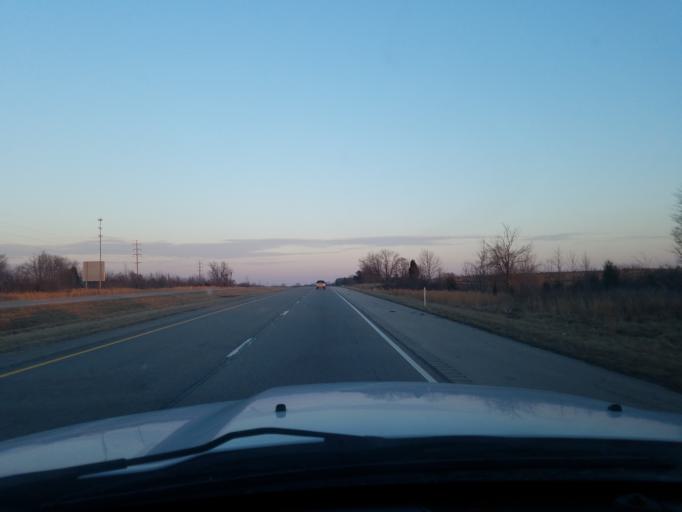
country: US
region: Indiana
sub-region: Warrick County
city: Boonville
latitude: 38.1995
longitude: -87.2685
